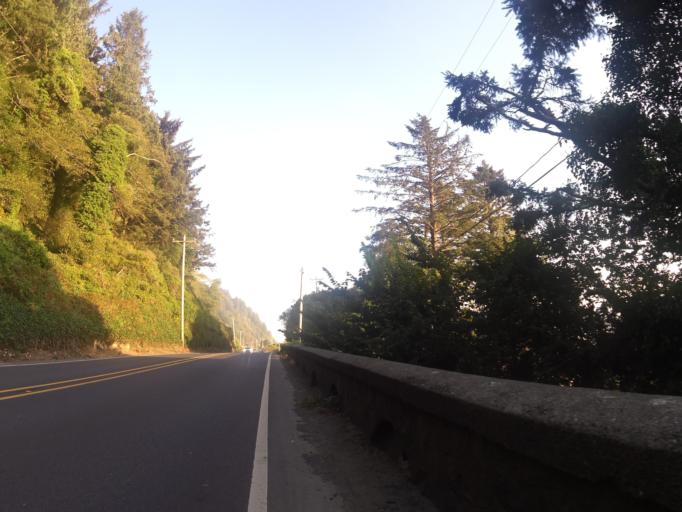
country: US
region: Oregon
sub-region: Tillamook County
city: Rockaway Beach
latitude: 45.5683
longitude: -123.9414
